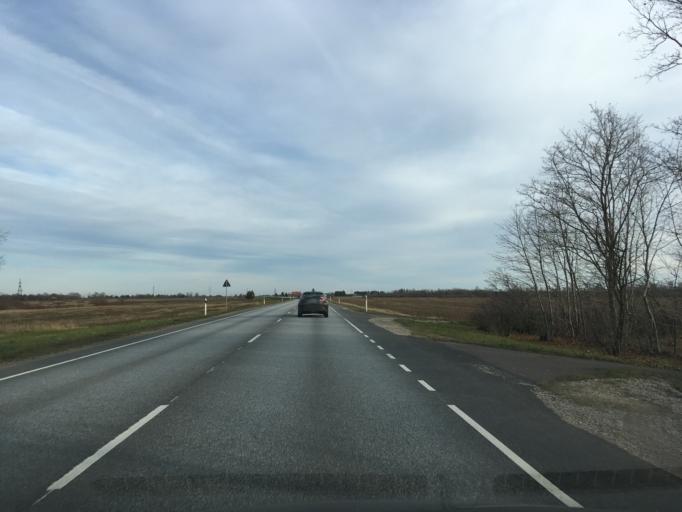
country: EE
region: Ida-Virumaa
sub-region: Narva-Joesuu linn
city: Narva-Joesuu
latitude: 59.3991
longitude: 28.0088
